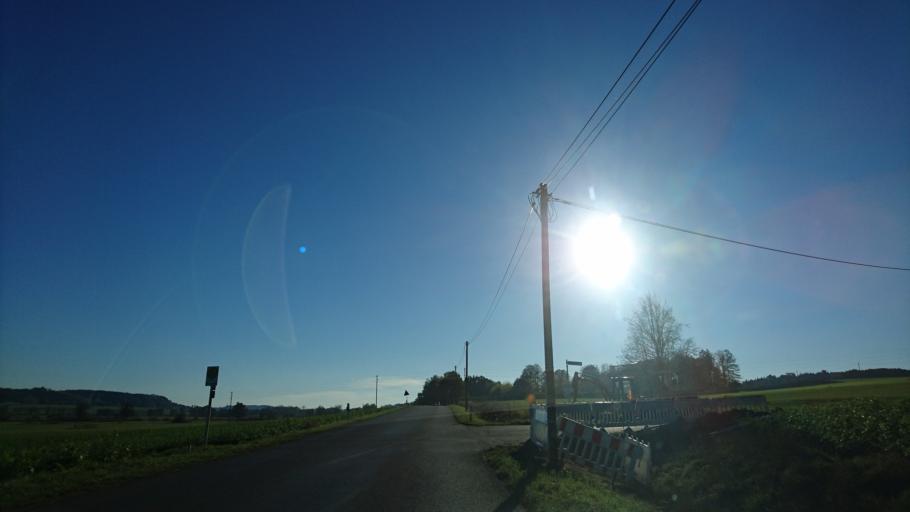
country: DE
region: Bavaria
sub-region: Swabia
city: Zusmarshausen
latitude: 48.4007
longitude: 10.5864
